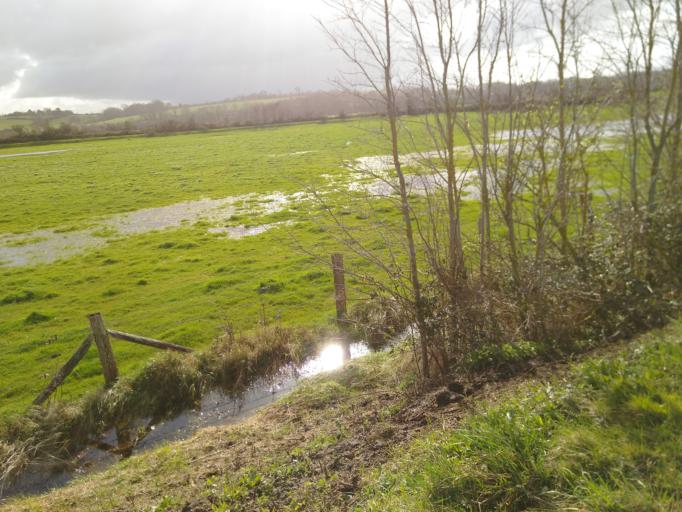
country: FR
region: Lower Normandy
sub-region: Departement du Calvados
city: Ouistreham
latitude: 49.2638
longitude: -0.2460
